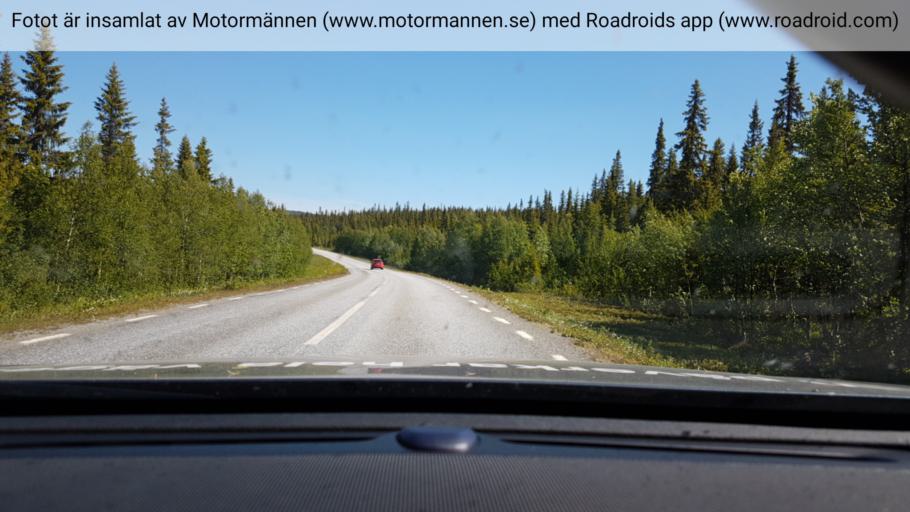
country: SE
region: Vaesterbotten
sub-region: Vilhelmina Kommun
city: Sjoberg
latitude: 64.9613
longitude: 15.4197
